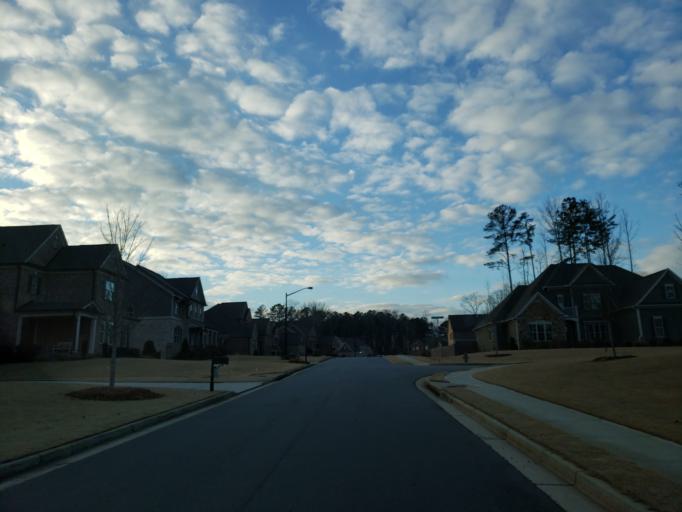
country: US
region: Georgia
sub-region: Cobb County
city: Acworth
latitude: 34.0220
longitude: -84.6803
